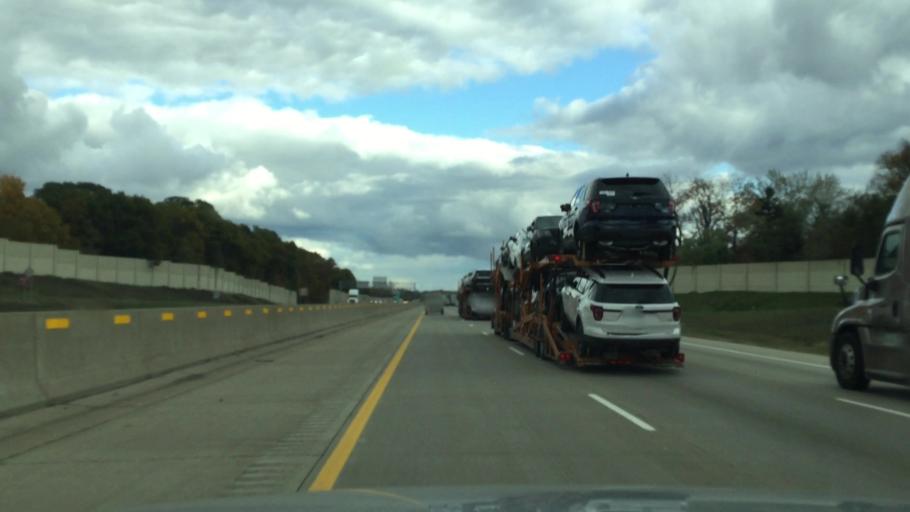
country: US
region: Michigan
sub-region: Kalamazoo County
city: Portage
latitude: 42.2378
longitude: -85.6129
